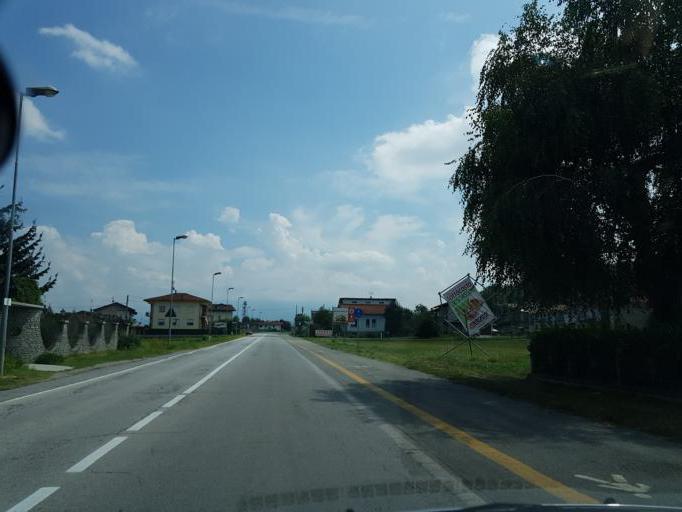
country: IT
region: Piedmont
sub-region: Provincia di Cuneo
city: Cervasca
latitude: 44.3787
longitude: 7.4720
